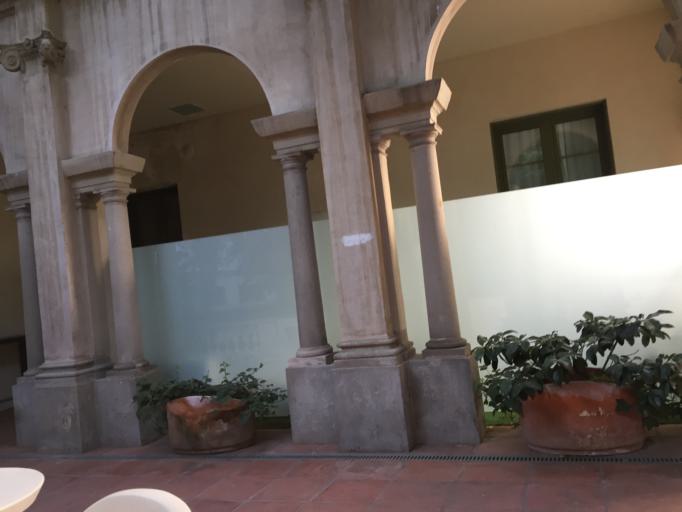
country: ES
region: Catalonia
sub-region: Provincia de Barcelona
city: Ciutat Vella
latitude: 41.3810
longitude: 2.1741
